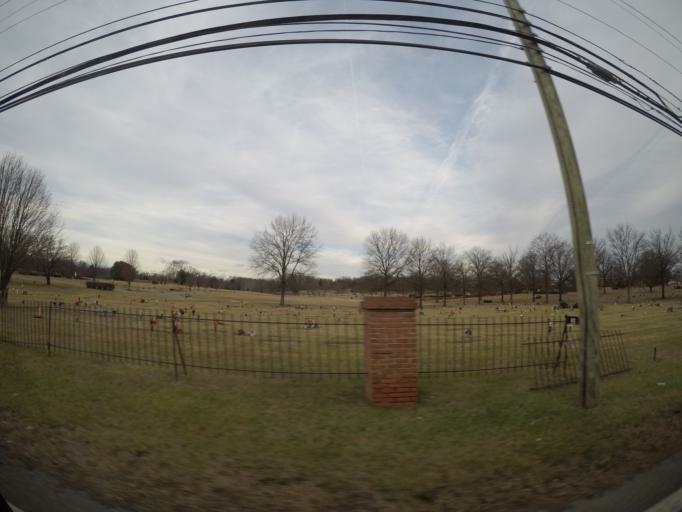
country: US
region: Maryland
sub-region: Anne Arundel County
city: Jessup
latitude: 39.1859
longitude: -76.7656
